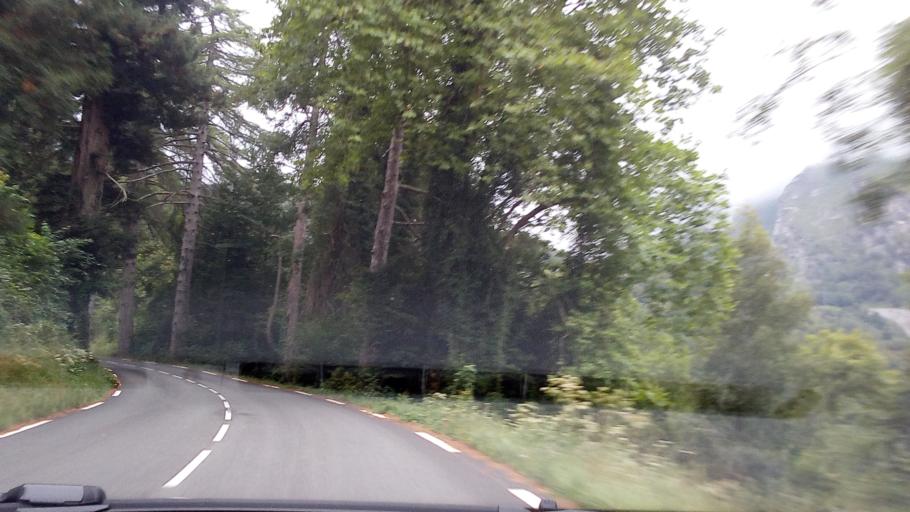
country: FR
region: Aquitaine
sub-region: Departement des Pyrenees-Atlantiques
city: Laruns
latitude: 42.9795
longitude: -0.4157
